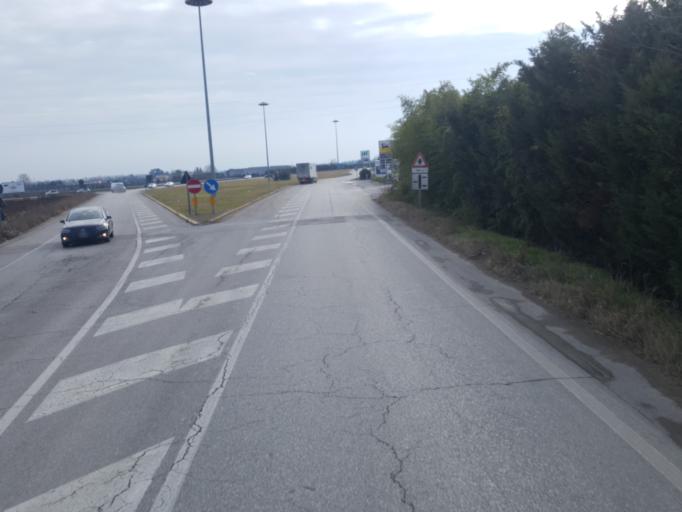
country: IT
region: Veneto
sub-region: Provincia di Verona
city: Sona
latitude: 45.4411
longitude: 10.8508
